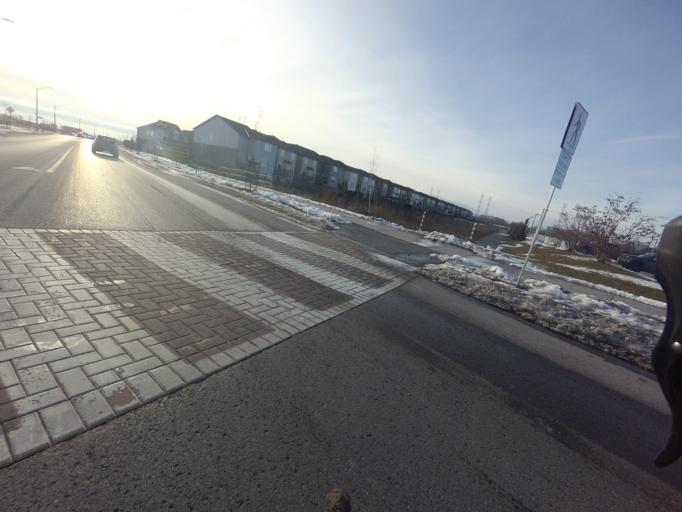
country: CA
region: Ontario
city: Bells Corners
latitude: 45.2797
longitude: -75.8686
